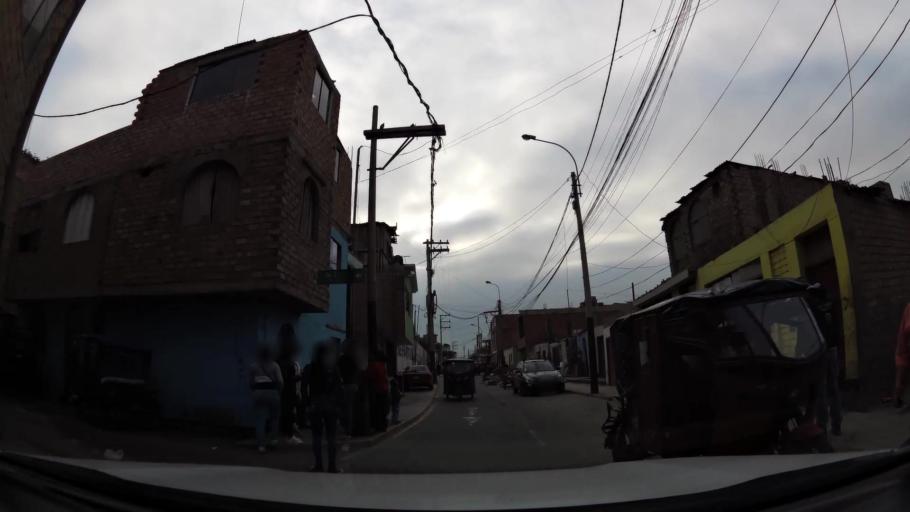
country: PE
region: Lima
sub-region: Lima
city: Surco
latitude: -12.1451
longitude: -77.0113
